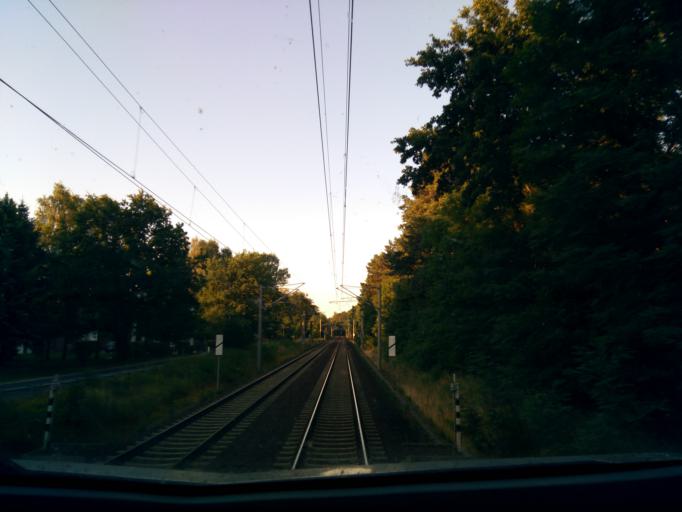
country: DE
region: Brandenburg
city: Bestensee
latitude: 52.2559
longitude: 13.6335
